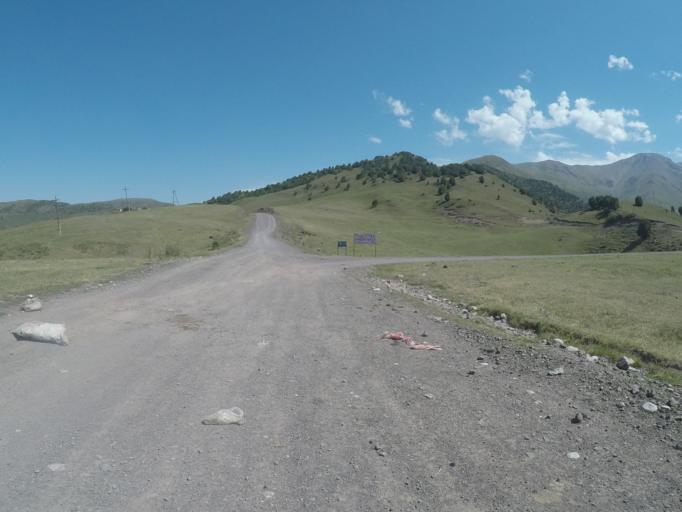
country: KG
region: Chuy
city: Bishkek
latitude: 42.6501
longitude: 74.5307
